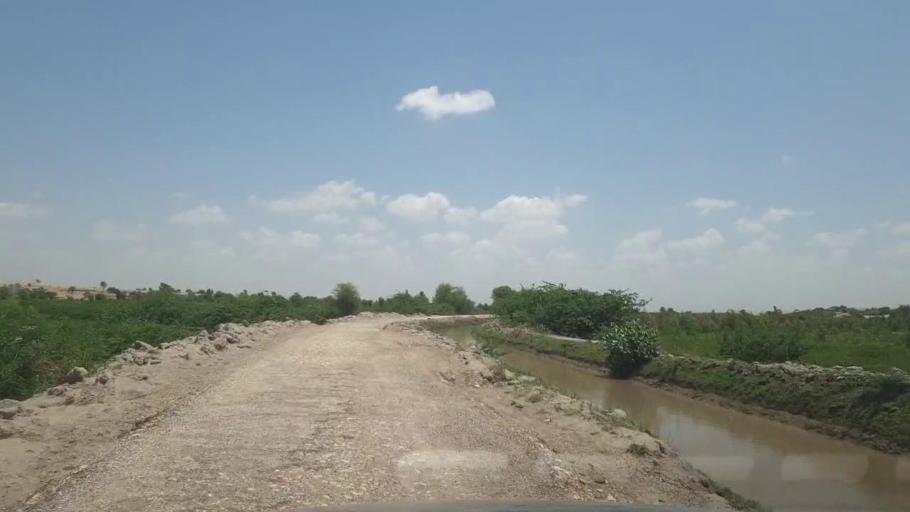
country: PK
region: Sindh
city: Kot Diji
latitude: 27.2954
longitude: 69.0727
